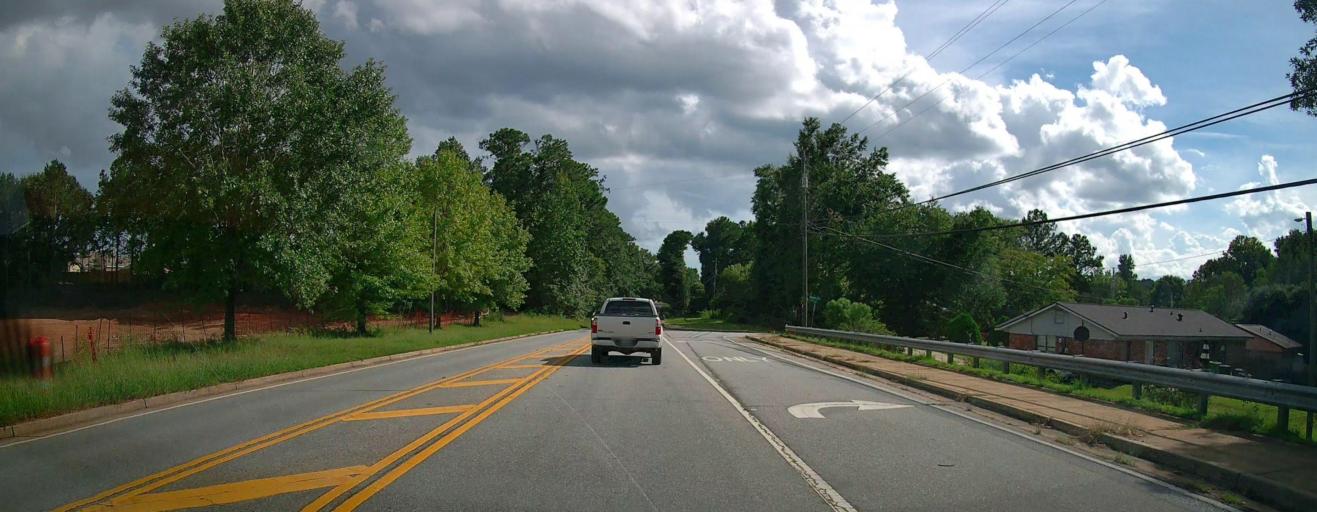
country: US
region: Alabama
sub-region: Russell County
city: Phenix City
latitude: 32.5688
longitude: -84.9693
